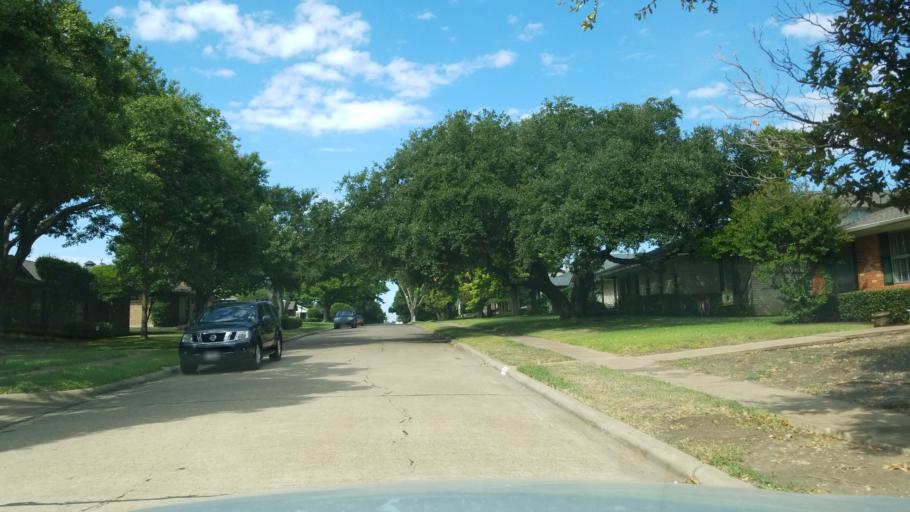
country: US
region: Texas
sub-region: Dallas County
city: Richardson
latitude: 32.9687
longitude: -96.7742
